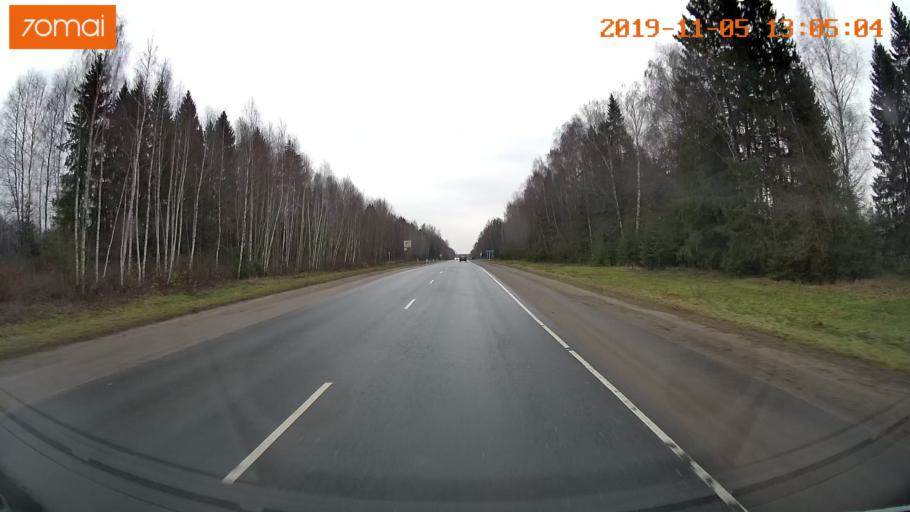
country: RU
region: Ivanovo
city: Kitovo
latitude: 56.8849
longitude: 41.2349
